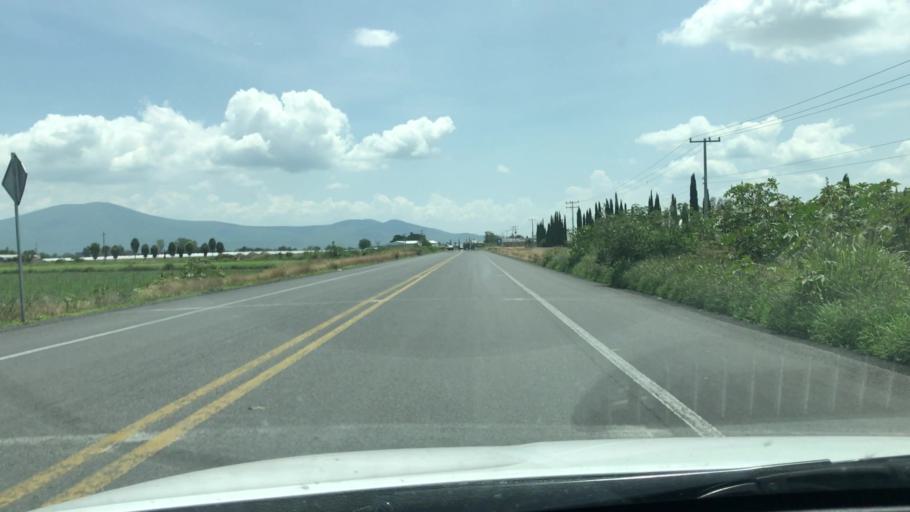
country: MX
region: Michoacan
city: Tanhuato de Guerrero
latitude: 20.2954
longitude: -102.3318
